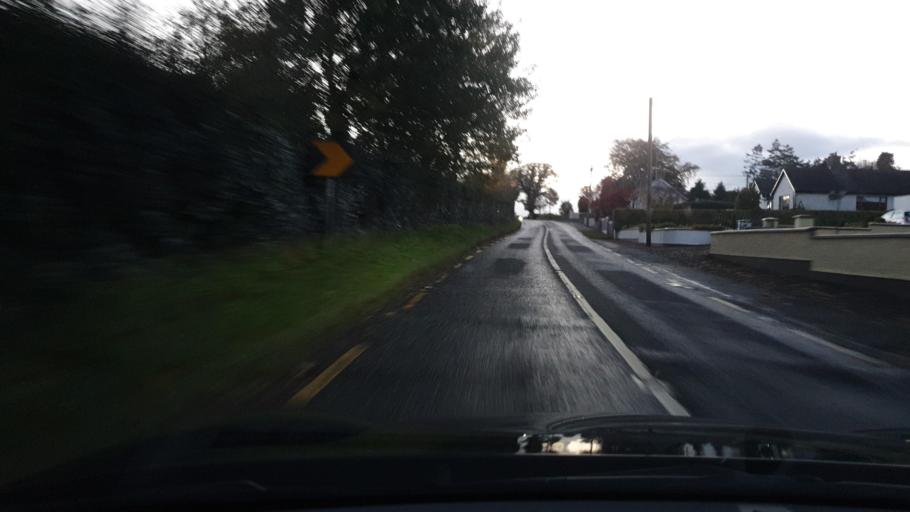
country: IE
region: Leinster
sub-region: An Mhi
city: Slane
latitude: 53.7083
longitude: -6.5170
